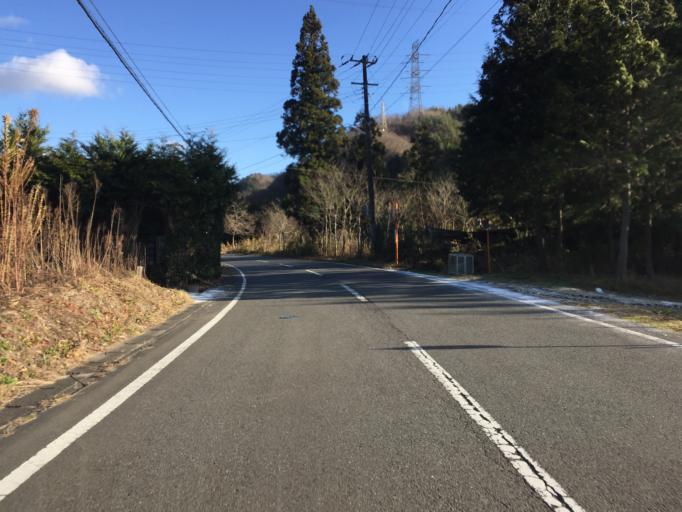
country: JP
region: Fukushima
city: Iwaki
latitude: 37.2024
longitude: 140.7613
